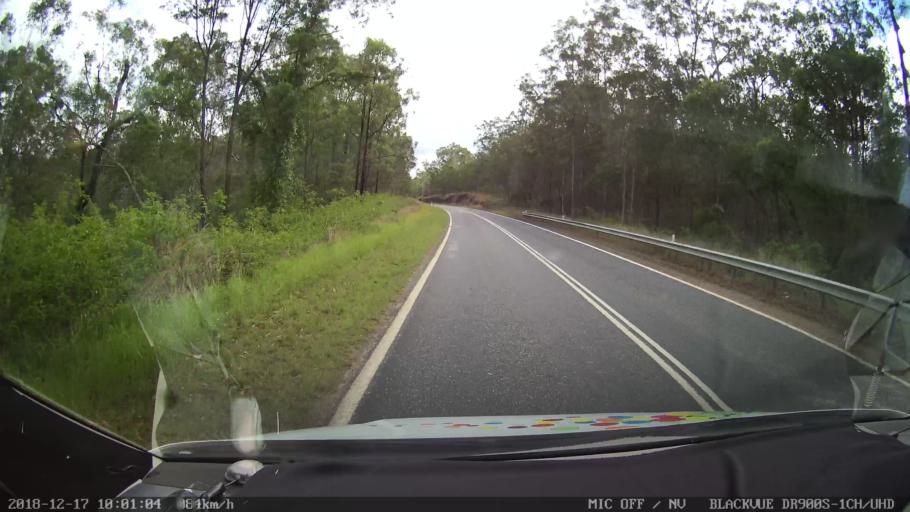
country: AU
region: New South Wales
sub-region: Tenterfield Municipality
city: Carrolls Creek
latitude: -28.9080
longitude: 152.4344
